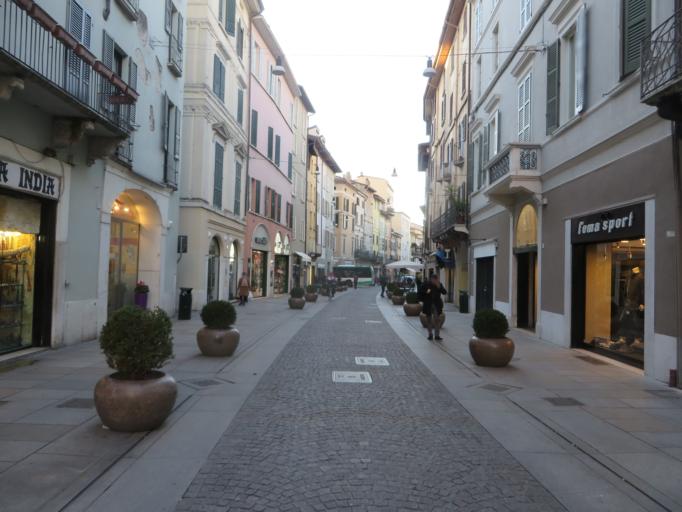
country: IT
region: Lombardy
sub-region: Provincia di Brescia
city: Brescia
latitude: 45.5407
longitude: 10.2152
